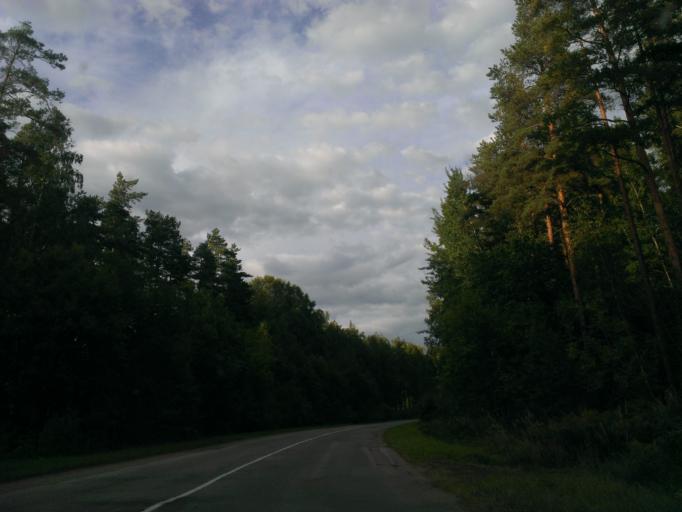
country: LV
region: Ikskile
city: Ikskile
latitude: 56.8517
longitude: 24.5038
